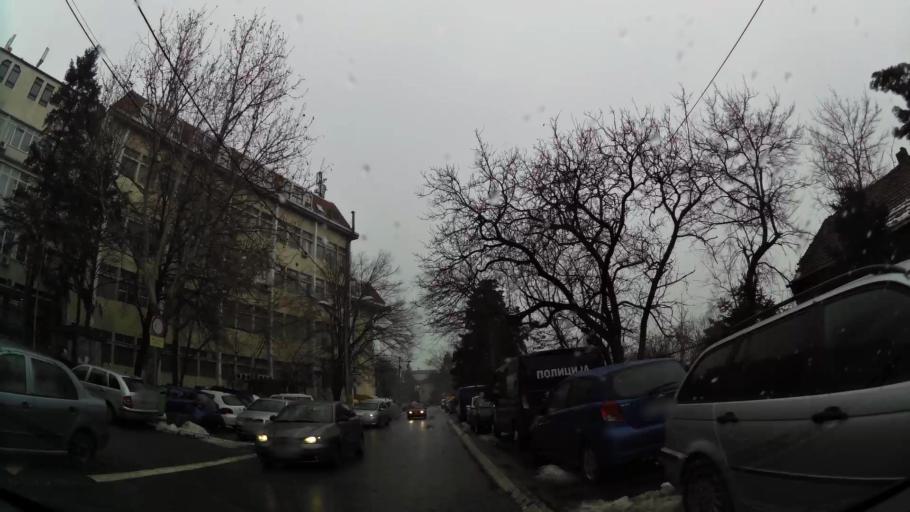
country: RS
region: Central Serbia
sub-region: Belgrade
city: Cukarica
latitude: 44.7832
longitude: 20.4153
